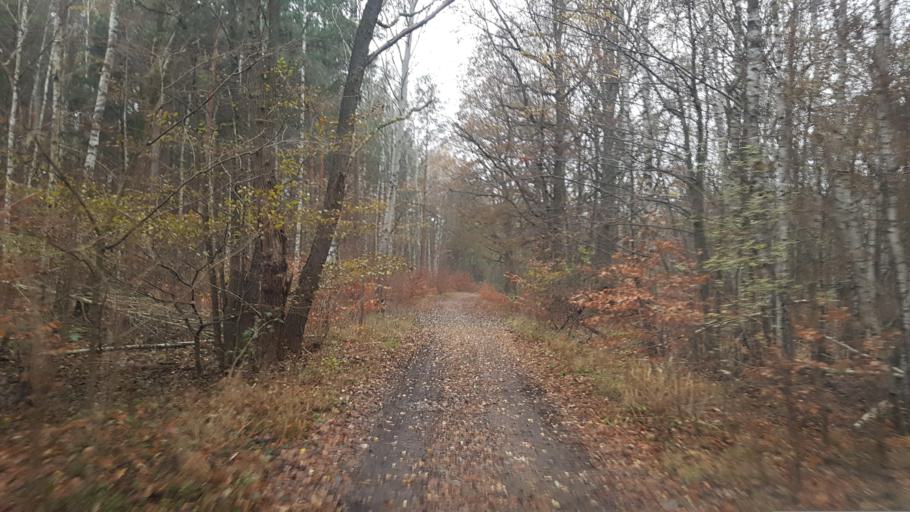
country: DE
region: Brandenburg
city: Crinitz
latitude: 51.7529
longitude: 13.7858
